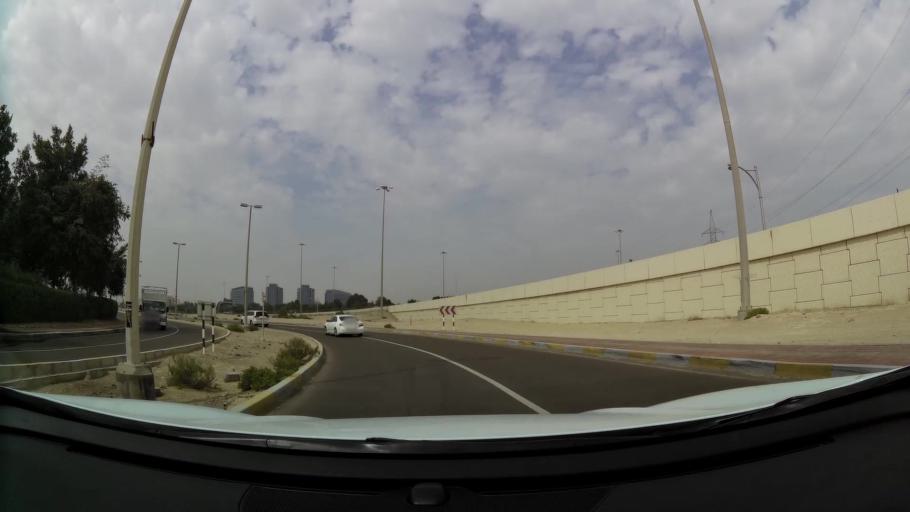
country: AE
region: Abu Dhabi
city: Abu Dhabi
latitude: 24.3250
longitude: 54.6227
